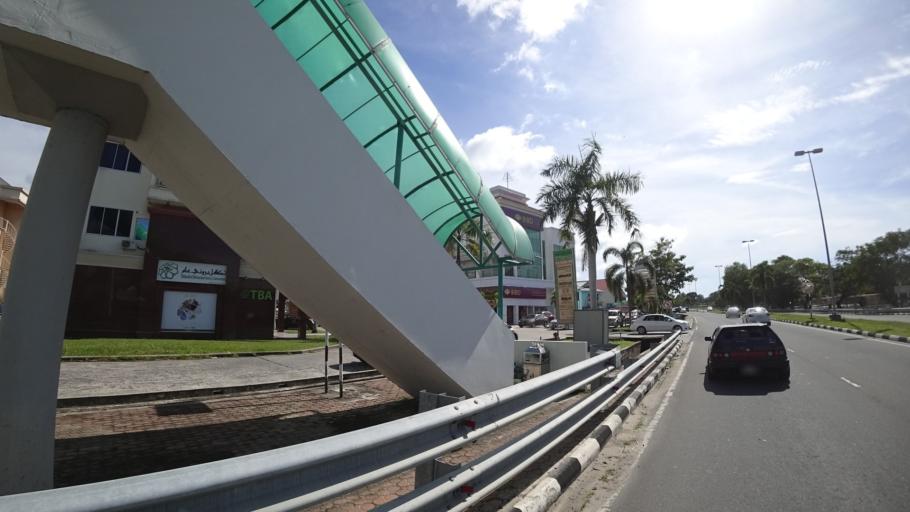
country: BN
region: Brunei and Muara
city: Bandar Seri Begawan
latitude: 4.9440
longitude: 114.9442
